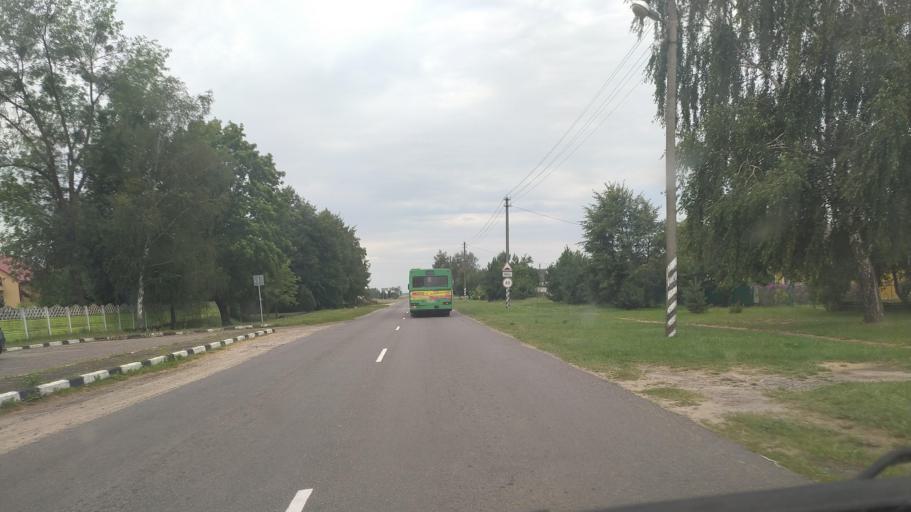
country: BY
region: Brest
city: Byaroza
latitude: 52.5797
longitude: 24.8577
